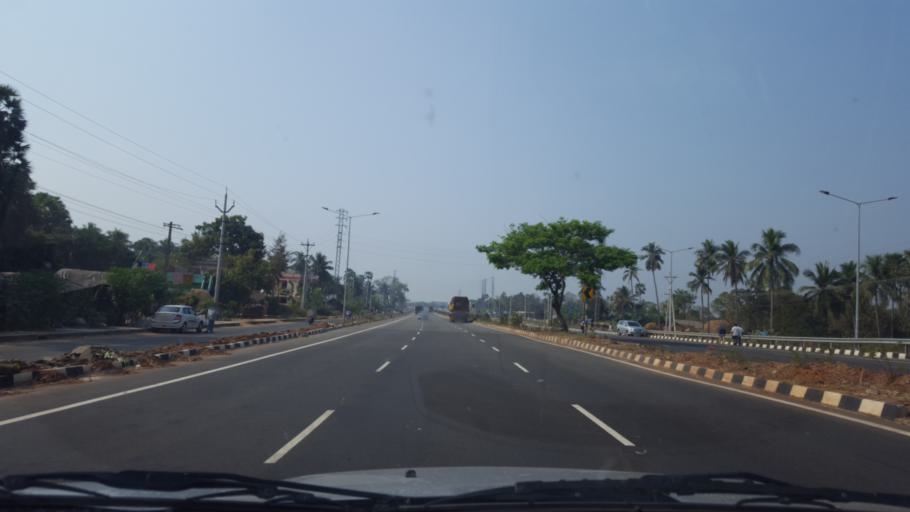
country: IN
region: Andhra Pradesh
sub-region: Vizianagaram District
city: Vizianagaram
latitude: 18.0268
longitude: 83.4910
